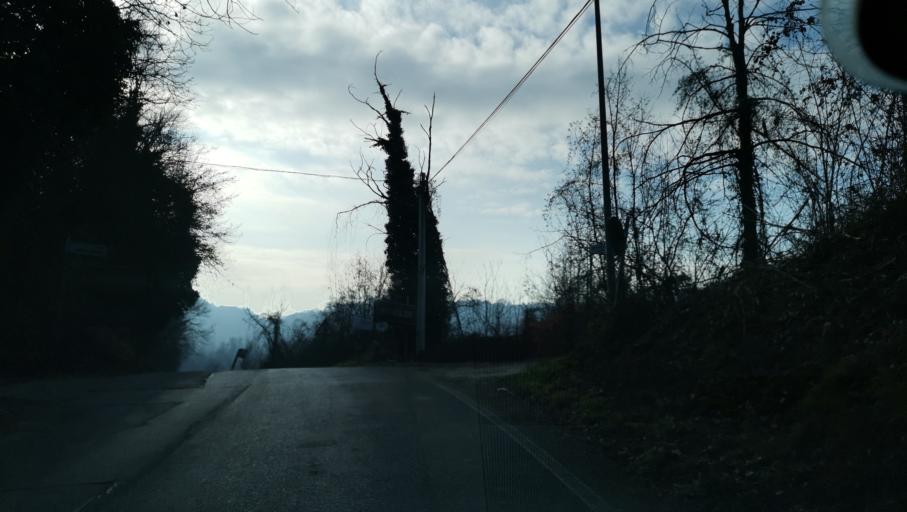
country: IT
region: Piedmont
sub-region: Provincia di Torino
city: Rivalba
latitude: 45.1088
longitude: 7.8859
